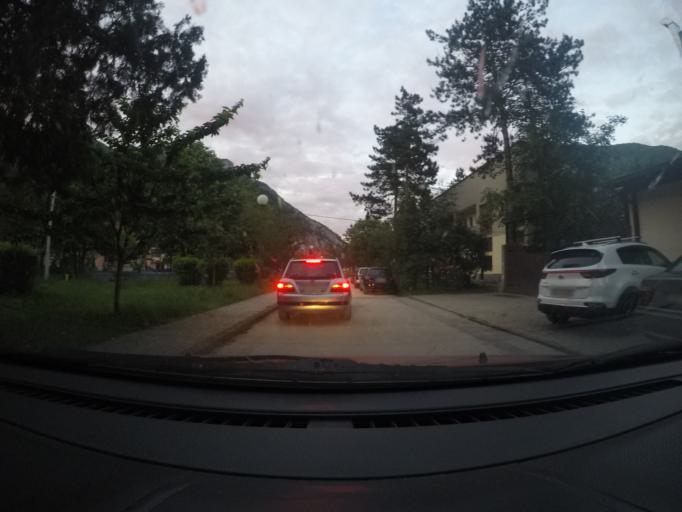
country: RS
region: Central Serbia
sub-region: Moravicki Okrug
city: Lucani
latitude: 43.8986
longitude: 20.1867
